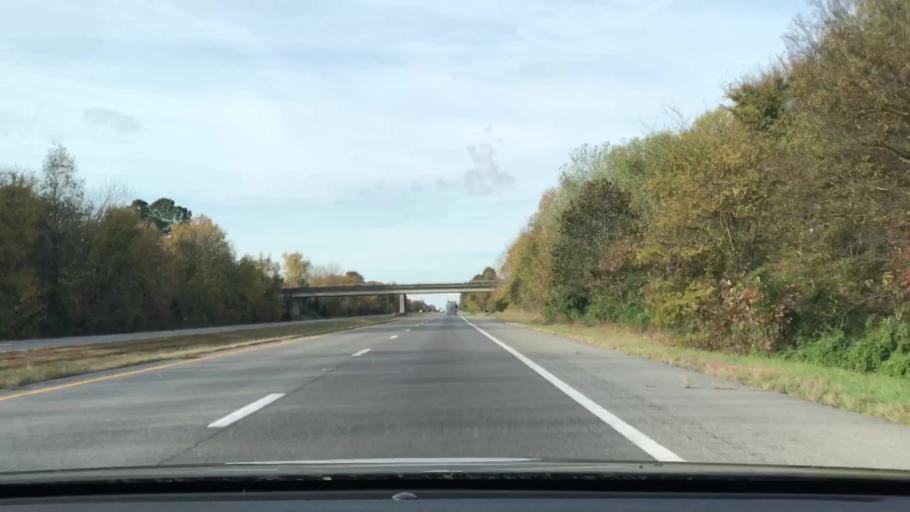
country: US
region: Kentucky
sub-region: Graves County
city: Mayfield
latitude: 36.7986
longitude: -88.5036
